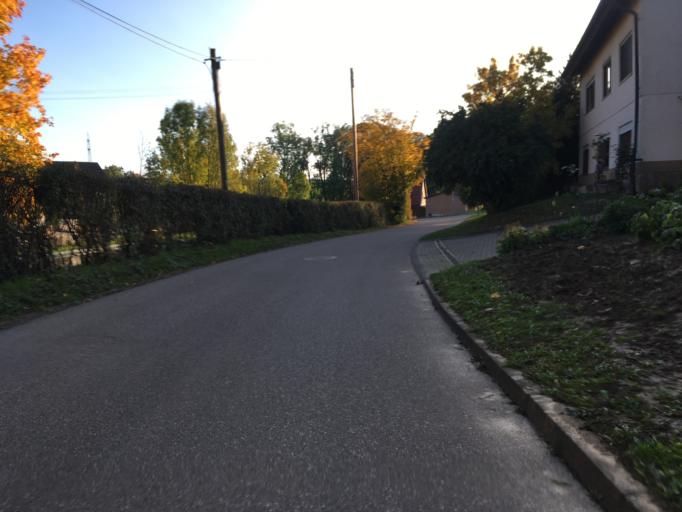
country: DE
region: Baden-Wuerttemberg
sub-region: Regierungsbezirk Stuttgart
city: Neuenstein
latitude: 49.2222
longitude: 9.6042
